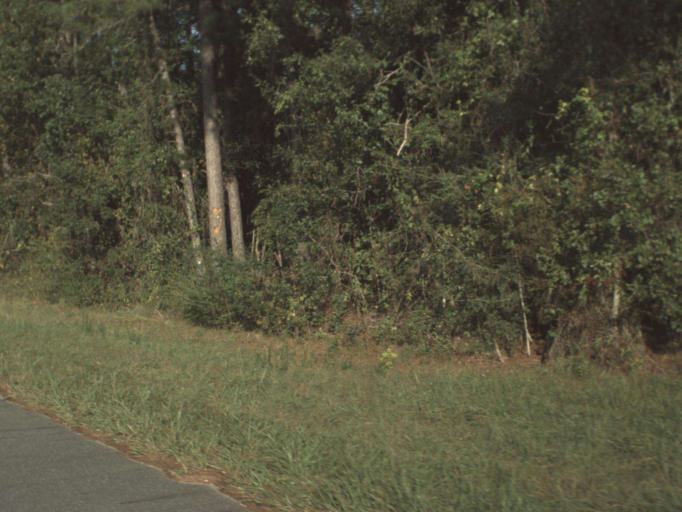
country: US
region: Florida
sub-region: Holmes County
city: Bonifay
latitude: 30.7019
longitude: -85.6229
